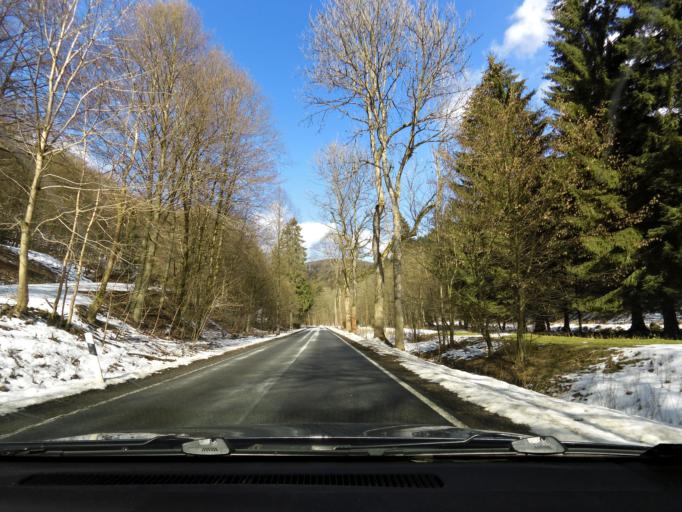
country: DE
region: Lower Saxony
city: Sankt Andreasberg
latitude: 51.6688
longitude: 10.5064
